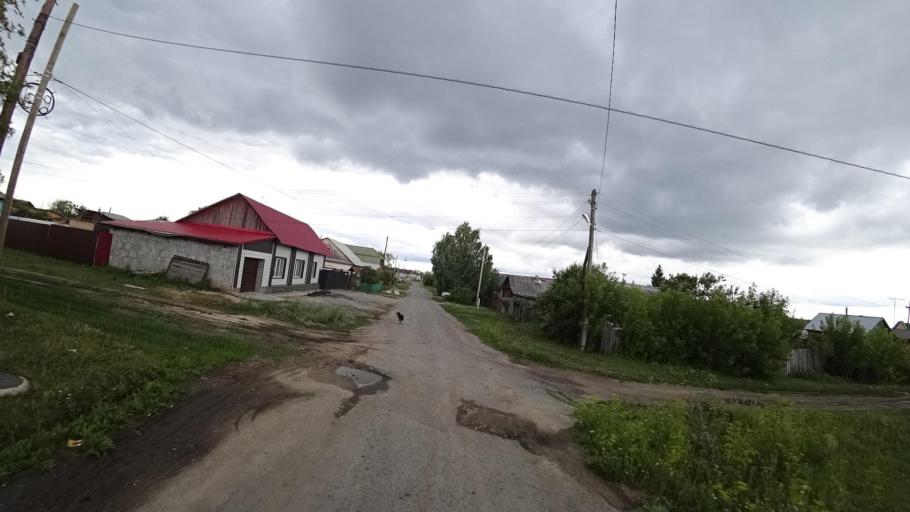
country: RU
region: Sverdlovsk
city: Kamyshlov
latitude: 56.8488
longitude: 62.7400
